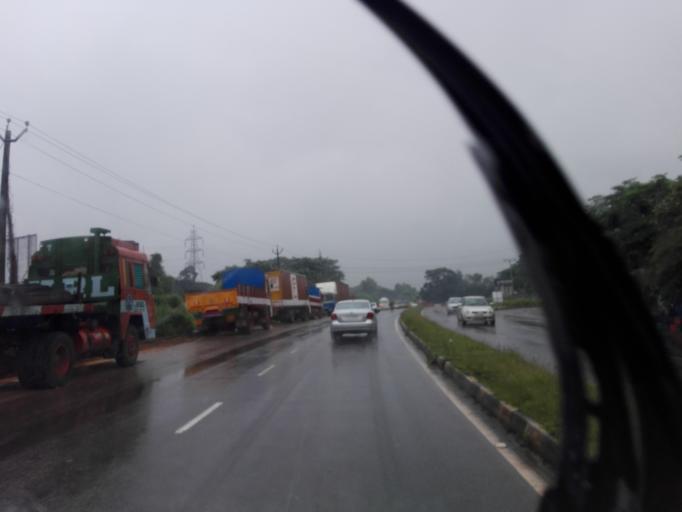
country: IN
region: Kerala
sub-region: Ernakulam
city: Elur
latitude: 10.0498
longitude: 76.3353
